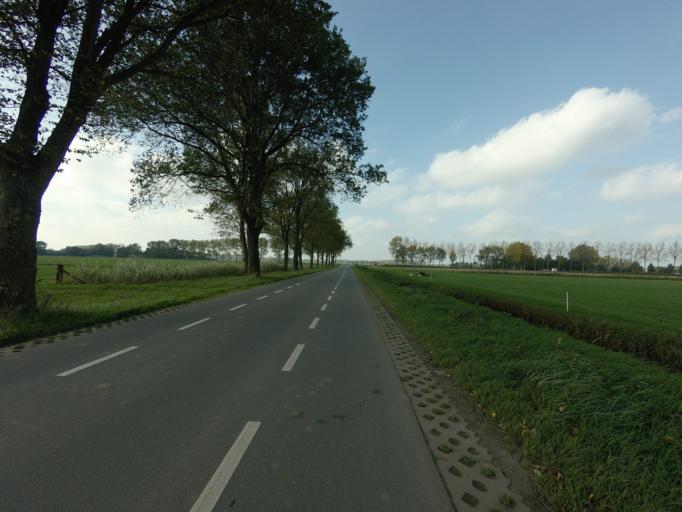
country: NL
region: Gelderland
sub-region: Gemeente Geldermalsen
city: Geldermalsen
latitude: 51.9212
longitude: 5.2876
